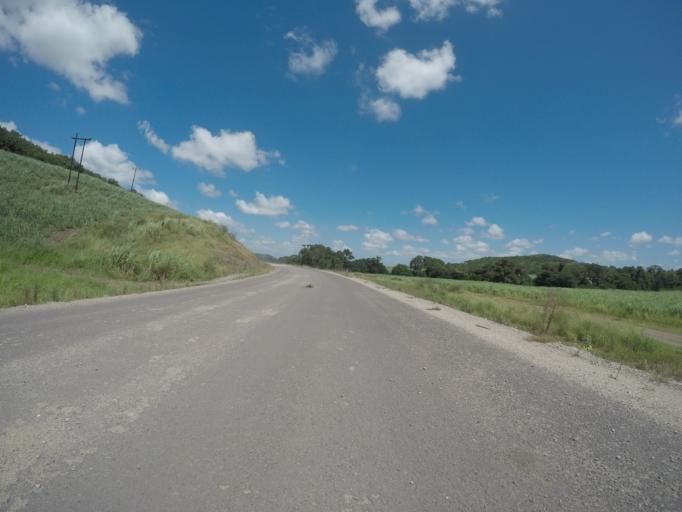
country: ZA
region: KwaZulu-Natal
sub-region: uThungulu District Municipality
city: Empangeni
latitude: -28.6538
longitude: 31.7688
